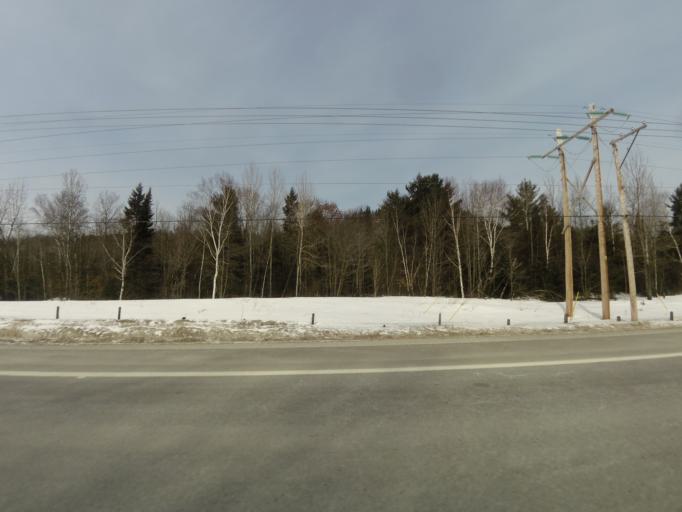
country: CA
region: Quebec
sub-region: Laurentides
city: Mont-Laurier
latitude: 46.2776
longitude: -75.6554
